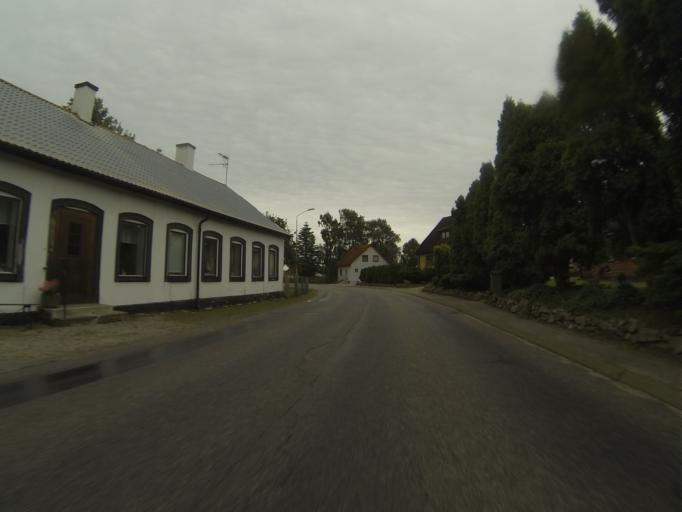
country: SE
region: Skane
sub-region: Lunds Kommun
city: Genarp
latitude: 55.6215
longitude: 13.3169
